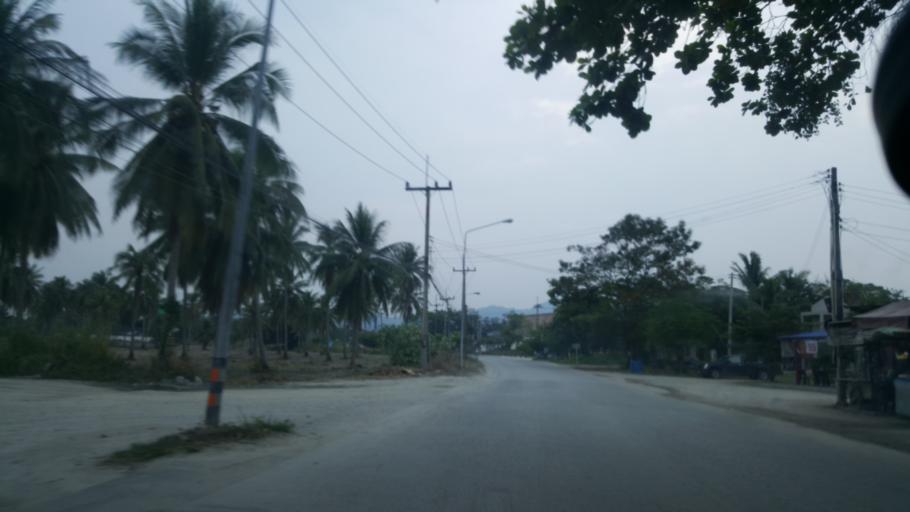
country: TH
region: Chon Buri
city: Si Racha
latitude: 13.2397
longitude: 101.0031
